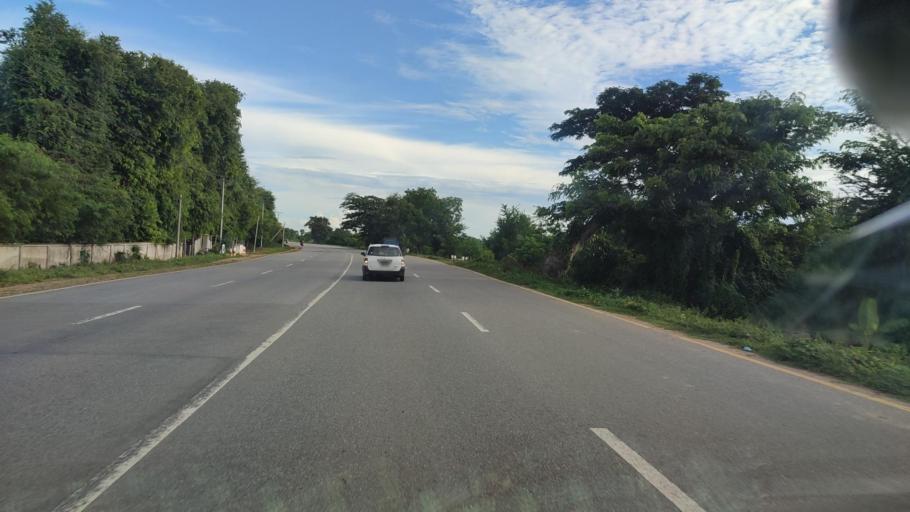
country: MM
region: Mandalay
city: Yamethin
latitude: 20.2049
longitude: 96.1805
